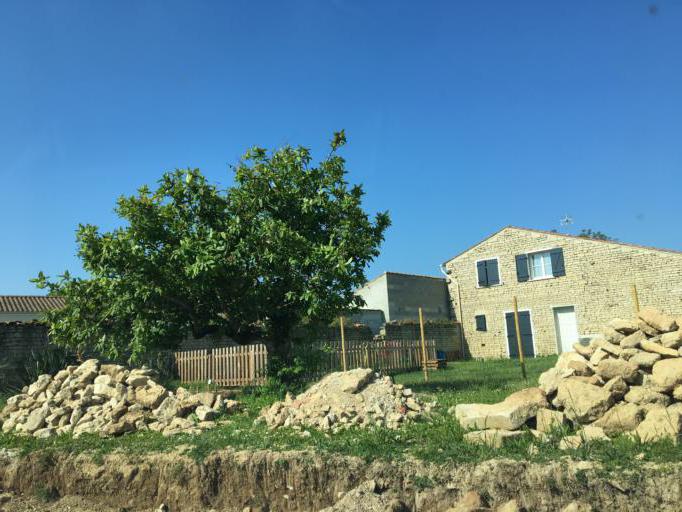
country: FR
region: Poitou-Charentes
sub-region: Departement des Deux-Sevres
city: Beauvoir-sur-Niort
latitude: 46.0754
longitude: -0.5082
